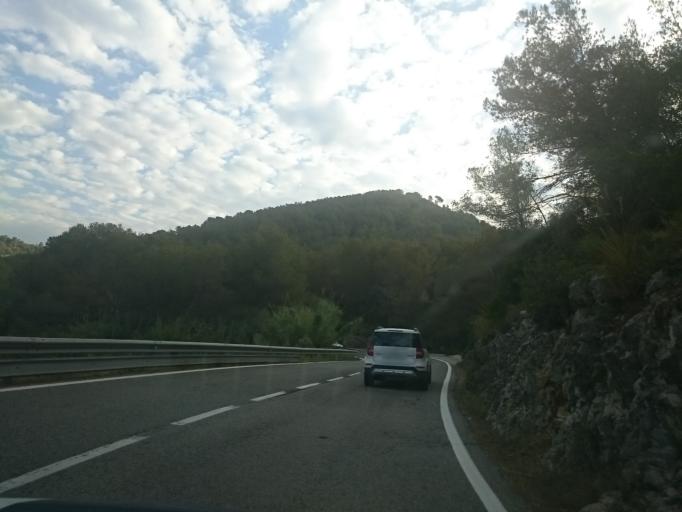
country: ES
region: Catalonia
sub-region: Provincia de Barcelona
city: Castellet
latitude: 41.2576
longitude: 1.6509
